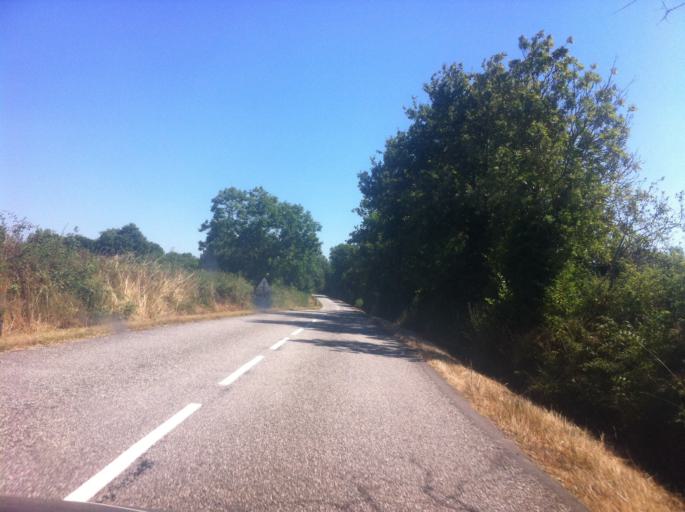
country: FR
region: Auvergne
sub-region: Departement de l'Allier
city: Montmarault
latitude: 46.2971
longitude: 3.0245
